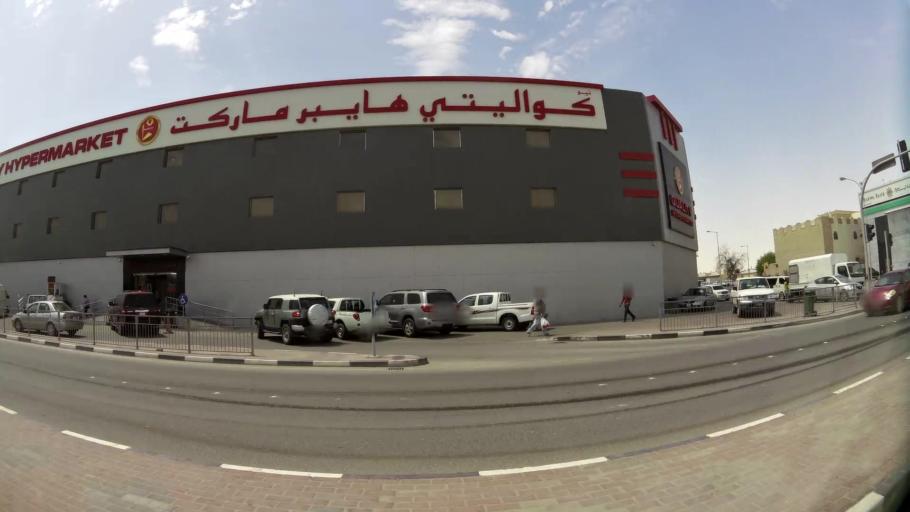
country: QA
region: Baladiyat ar Rayyan
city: Ar Rayyan
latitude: 25.2994
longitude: 51.4202
